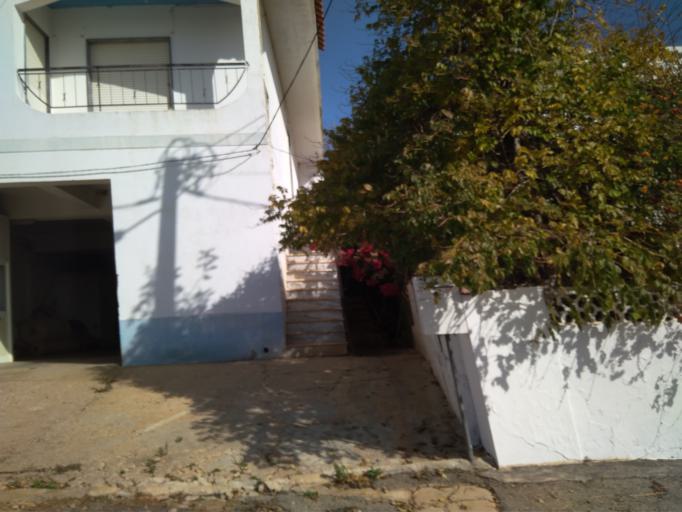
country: PT
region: Faro
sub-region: Faro
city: Santa Barbara de Nexe
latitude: 37.0691
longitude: -7.9572
